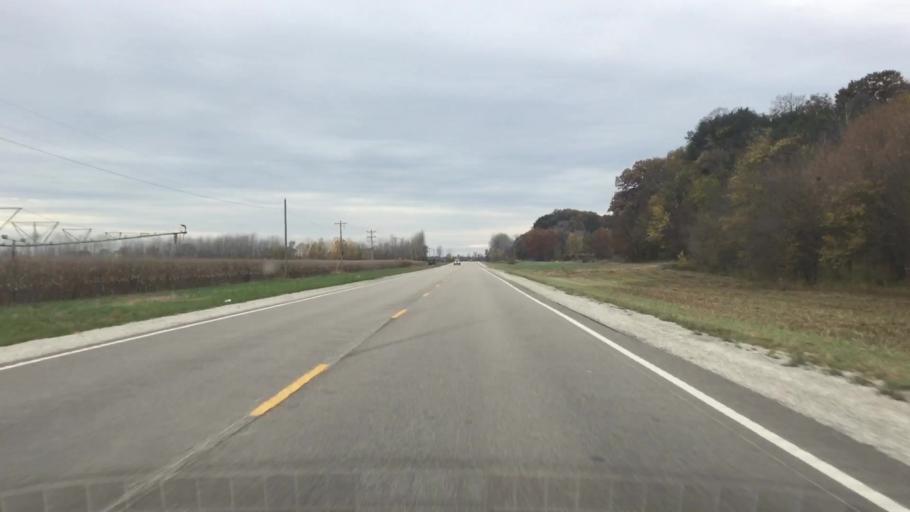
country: US
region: Missouri
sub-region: Callaway County
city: Holts Summit
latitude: 38.5816
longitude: -92.1039
